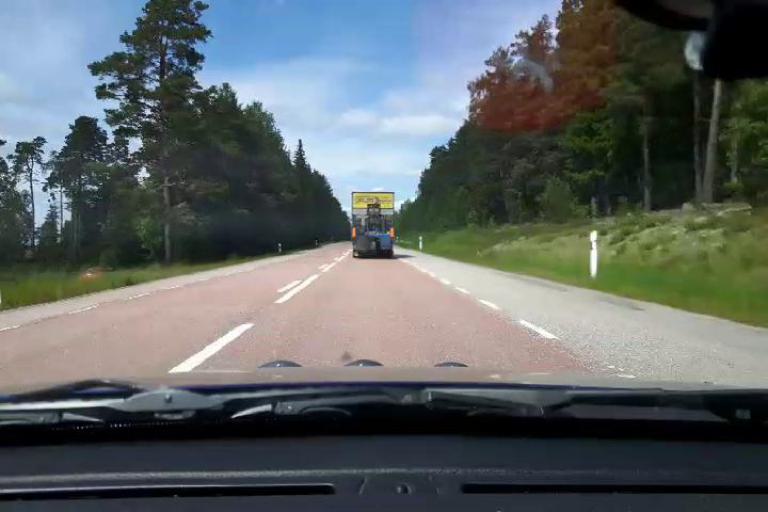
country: SE
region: Uppsala
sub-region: Osthammars Kommun
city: Bjorklinge
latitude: 60.1361
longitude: 17.5070
